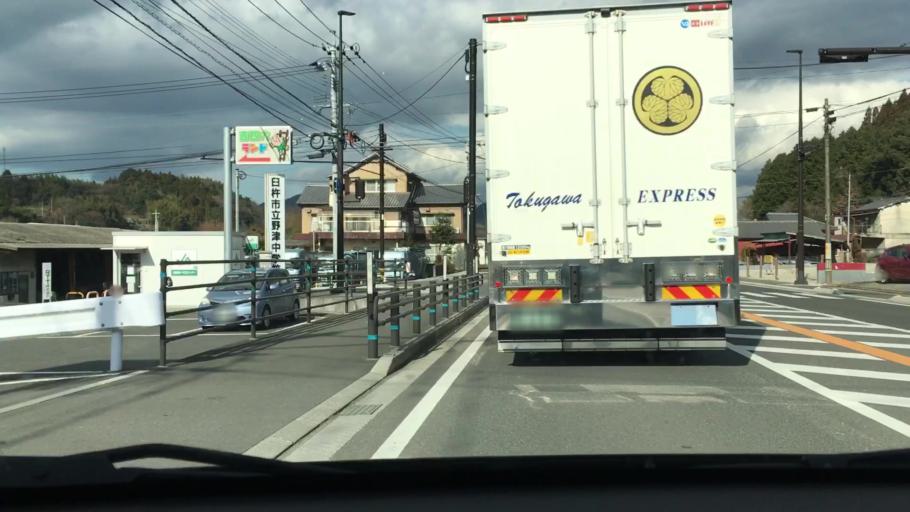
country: JP
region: Oita
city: Usuki
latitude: 33.0376
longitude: 131.6895
